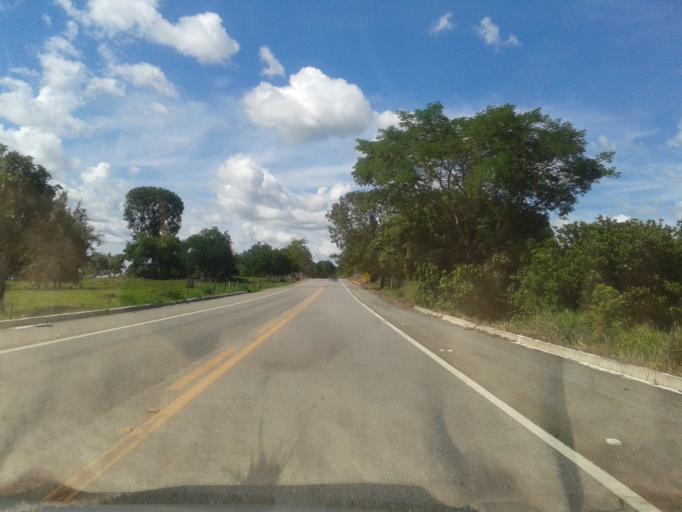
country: BR
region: Goias
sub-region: Itapuranga
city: Itapuranga
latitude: -15.6453
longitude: -50.2244
